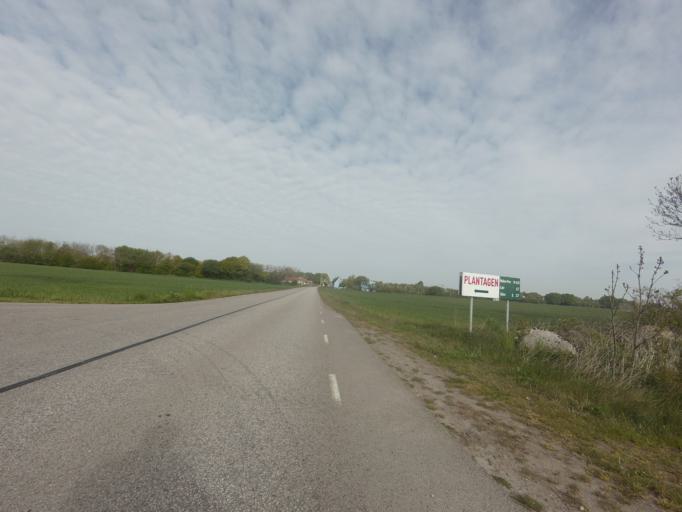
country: SE
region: Skane
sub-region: Hoganas Kommun
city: Hoganas
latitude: 56.1877
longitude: 12.5869
